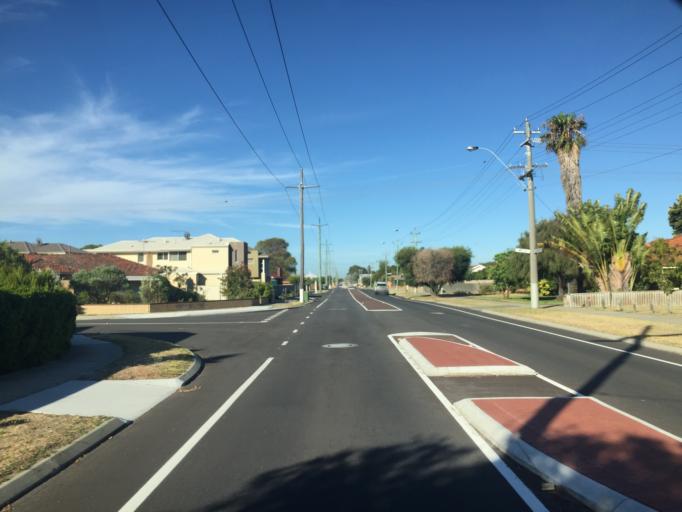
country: AU
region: Western Australia
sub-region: Belmont
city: Rivervale
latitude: -31.9635
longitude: 115.9254
